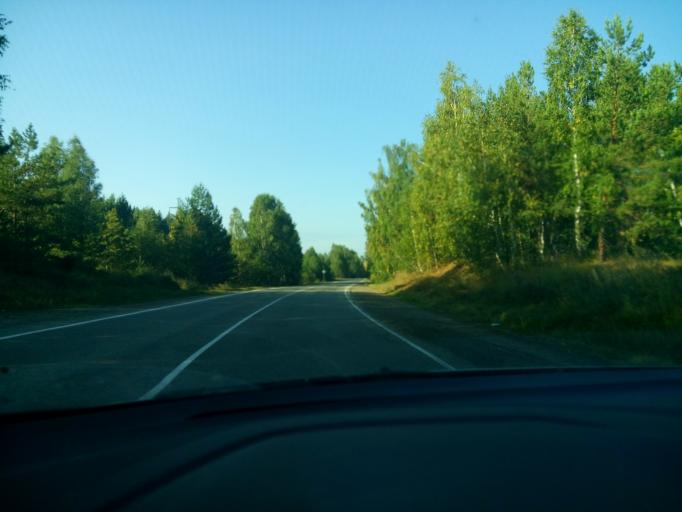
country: RU
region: Chelyabinsk
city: Kasli
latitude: 55.8676
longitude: 60.6975
